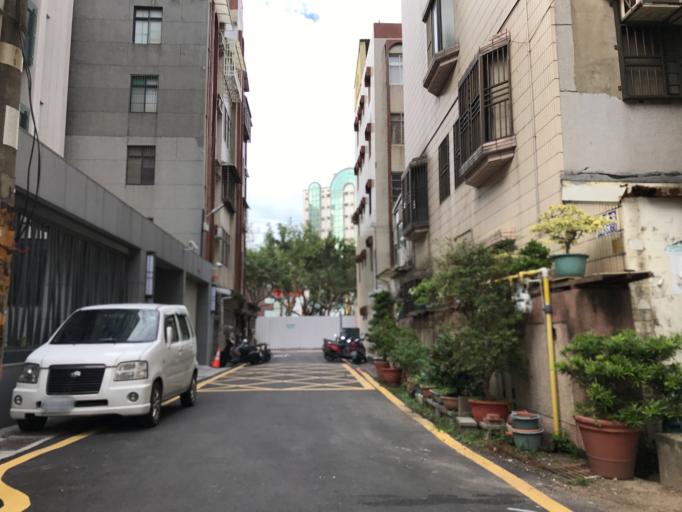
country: TW
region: Taiwan
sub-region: Hsinchu
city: Hsinchu
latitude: 24.8129
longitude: 120.9692
